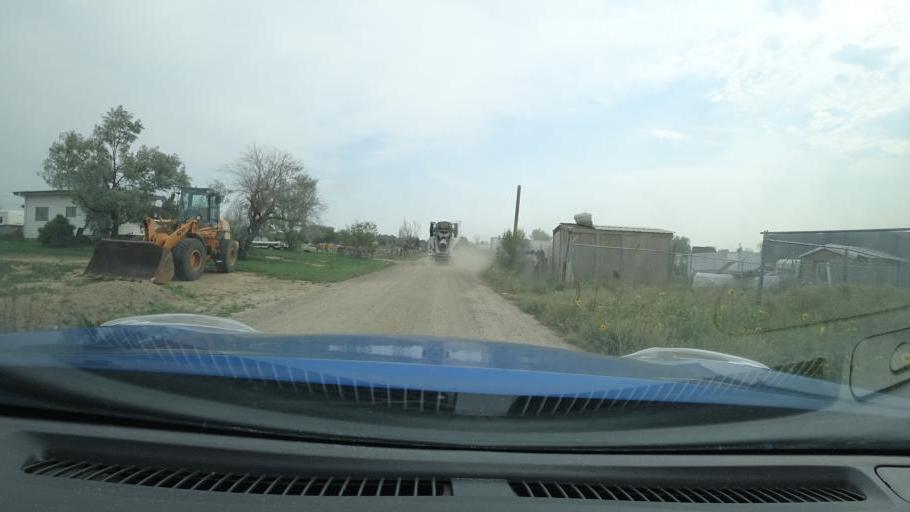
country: US
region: Colorado
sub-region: Adams County
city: Aurora
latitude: 39.7532
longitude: -104.7705
